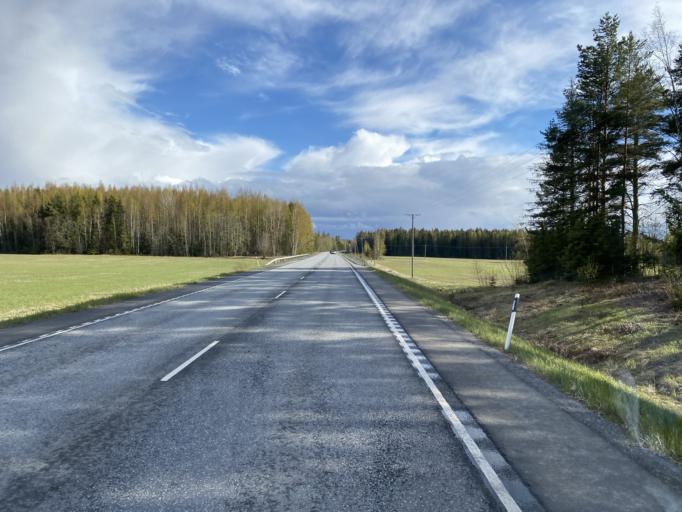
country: FI
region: Pirkanmaa
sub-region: Tampere
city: Lempaeaelae
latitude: 61.2807
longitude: 23.7448
